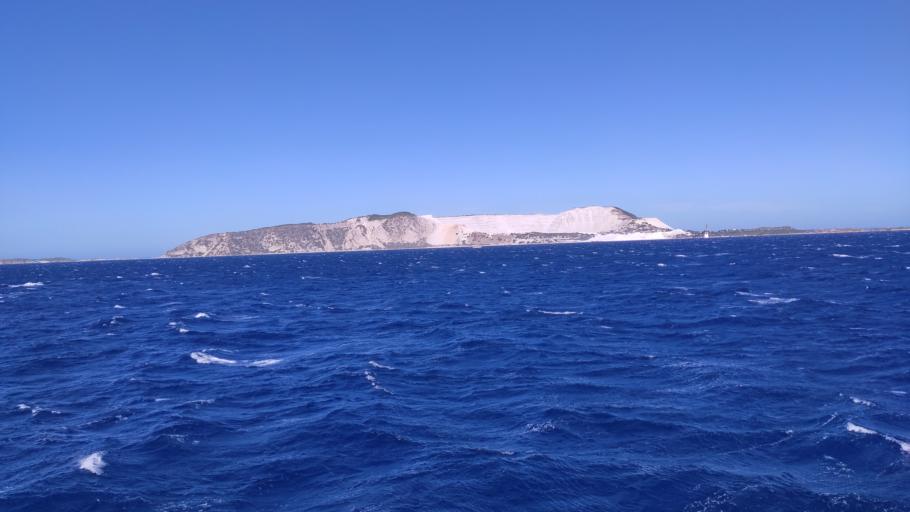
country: GR
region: South Aegean
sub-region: Nomos Dodekanisou
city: Mandraki
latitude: 36.6498
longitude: 27.1438
